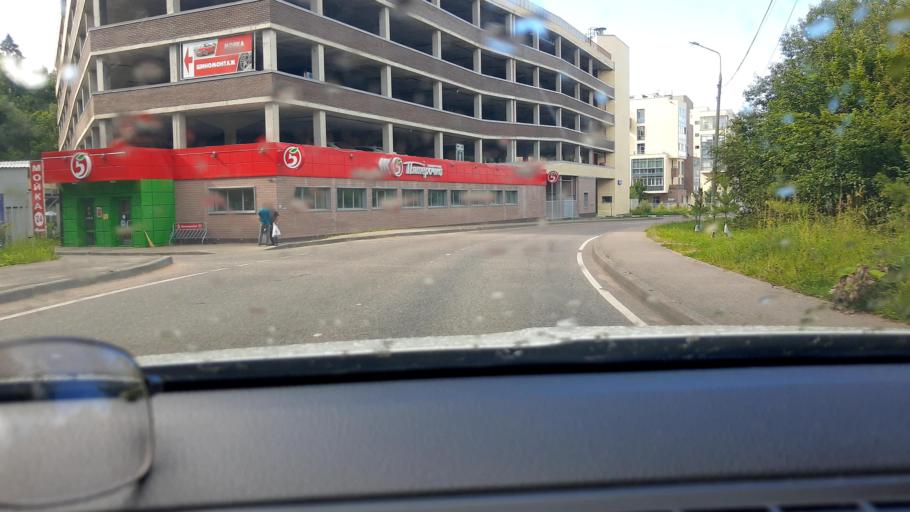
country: RU
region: Moskovskaya
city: Povedniki
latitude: 55.9749
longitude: 37.6065
